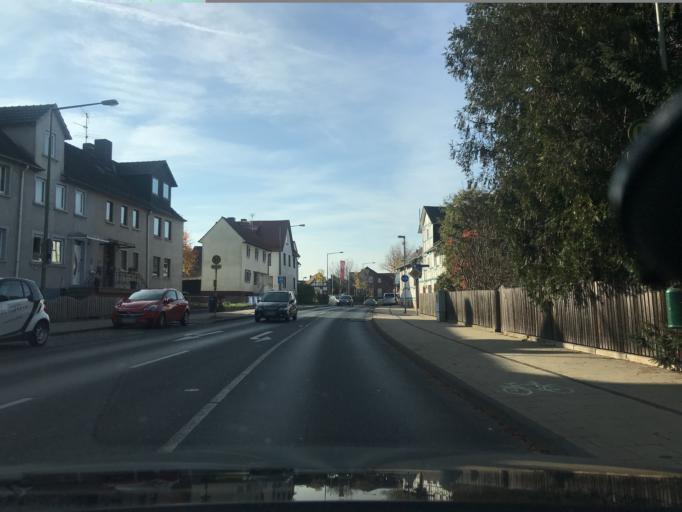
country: DE
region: Hesse
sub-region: Regierungsbezirk Kassel
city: Fuldabruck
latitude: 51.2760
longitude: 9.4527
